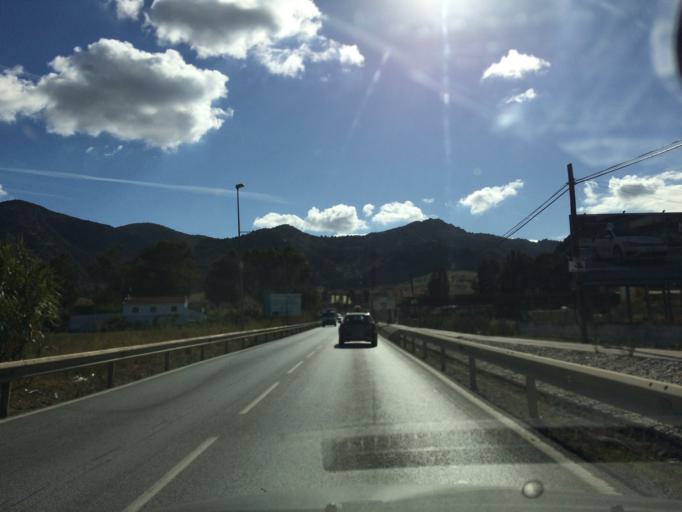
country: ES
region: Andalusia
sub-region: Provincia de Malaga
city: Estacion de Cartama
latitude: 36.7249
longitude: -4.6152
